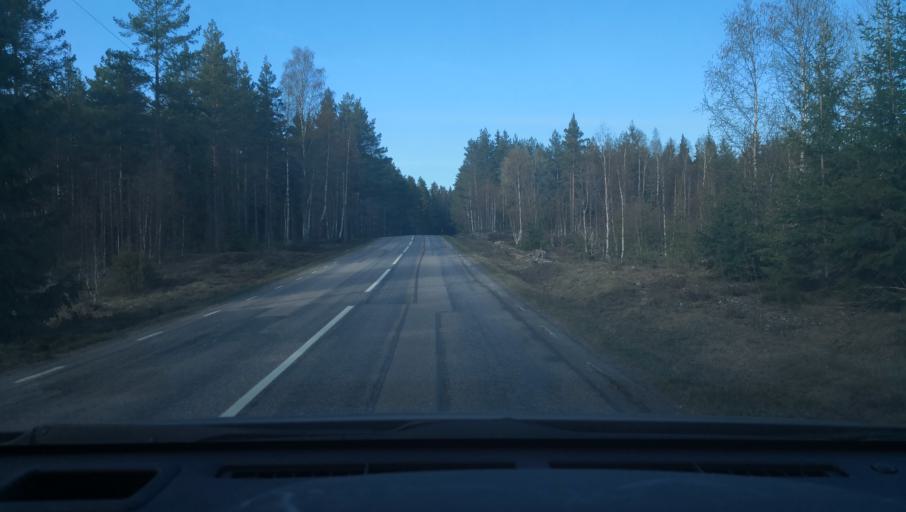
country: SE
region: Uppsala
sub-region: Heby Kommun
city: Morgongava
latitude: 59.9971
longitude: 16.9266
